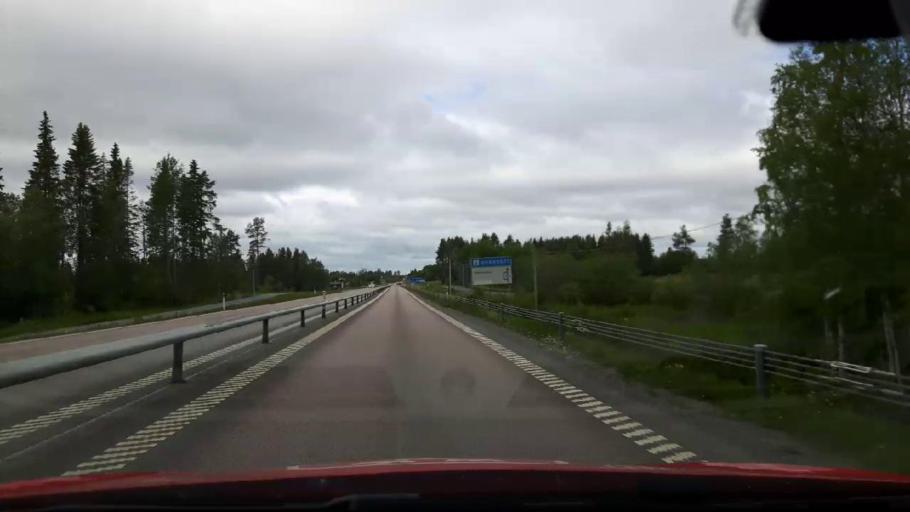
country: SE
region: Jaemtland
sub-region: Krokoms Kommun
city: Krokom
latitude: 63.2817
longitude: 14.5214
